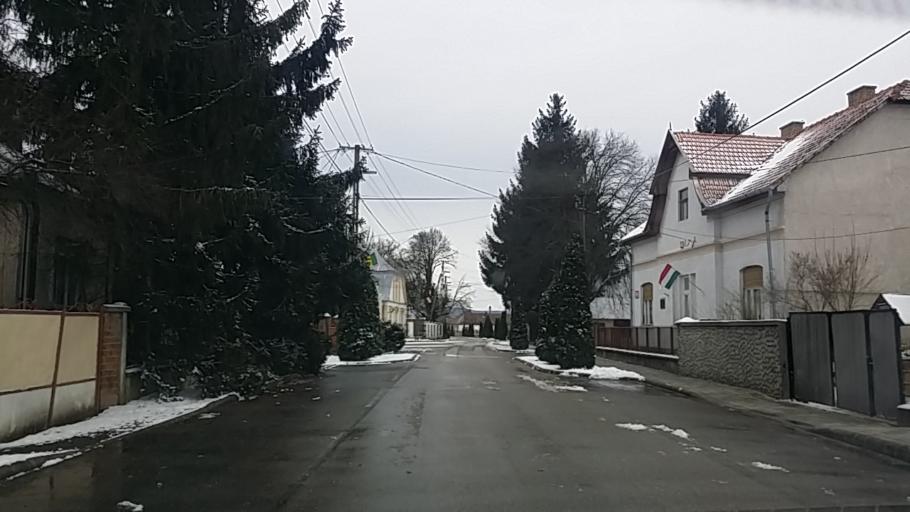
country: HU
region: Borsod-Abauj-Zemplen
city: Szendro
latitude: 48.4062
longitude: 20.7275
